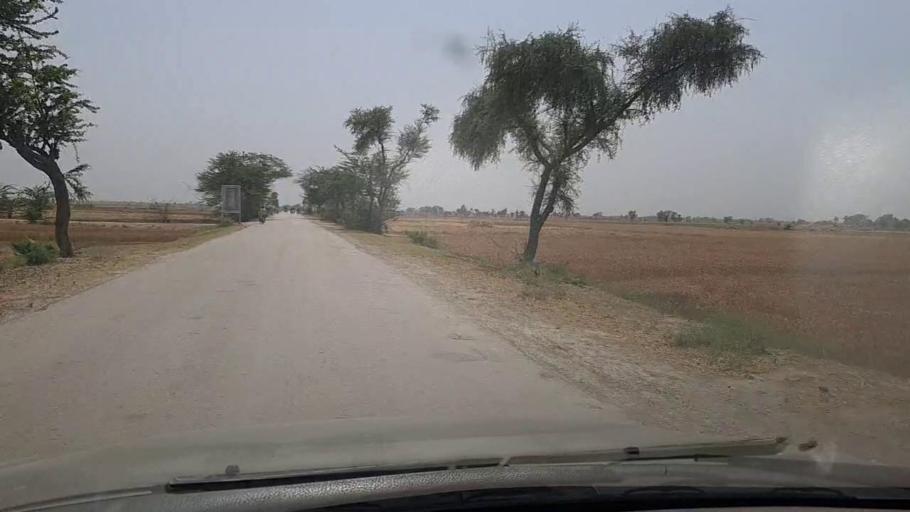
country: PK
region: Sindh
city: Miro Khan
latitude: 27.7012
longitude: 68.0610
